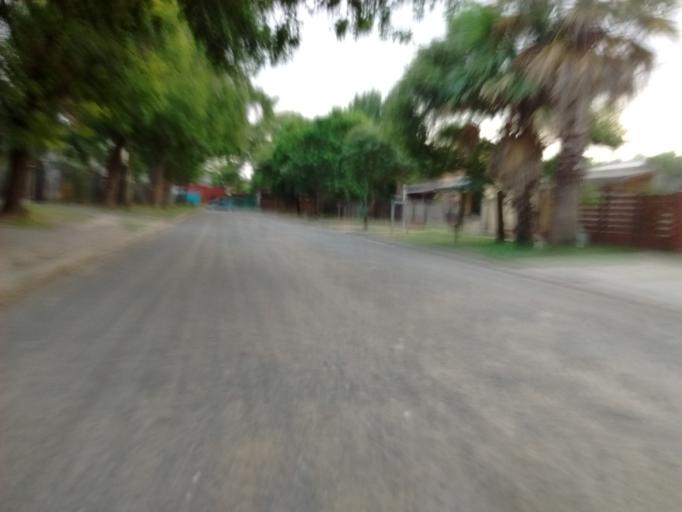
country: AR
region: Santa Fe
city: Funes
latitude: -32.9115
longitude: -60.8113
